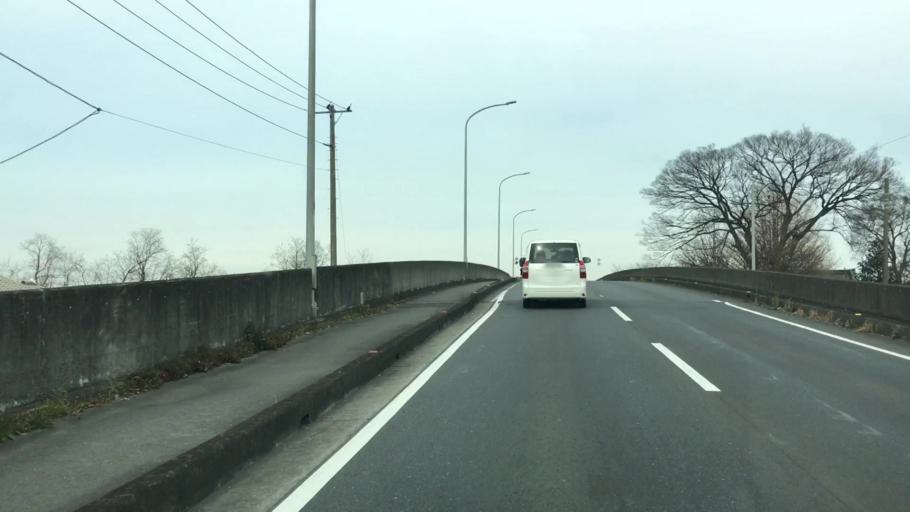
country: JP
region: Saitama
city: Kumagaya
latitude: 36.1333
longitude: 139.3236
